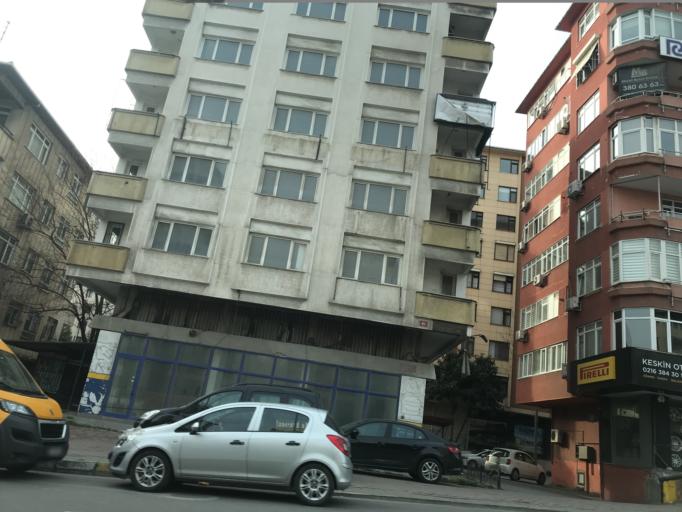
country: TR
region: Istanbul
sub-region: Atasehir
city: Atasehir
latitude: 40.9625
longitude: 29.1035
